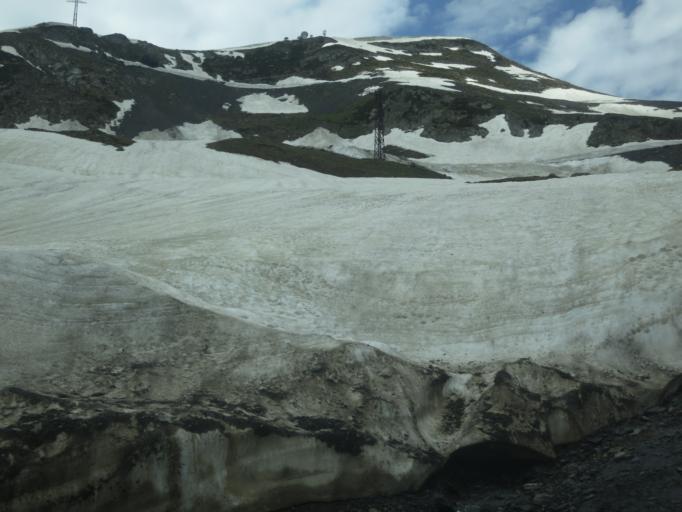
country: GE
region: Kakheti
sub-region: Telavi
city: Telavi
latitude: 42.2819
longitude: 45.5091
